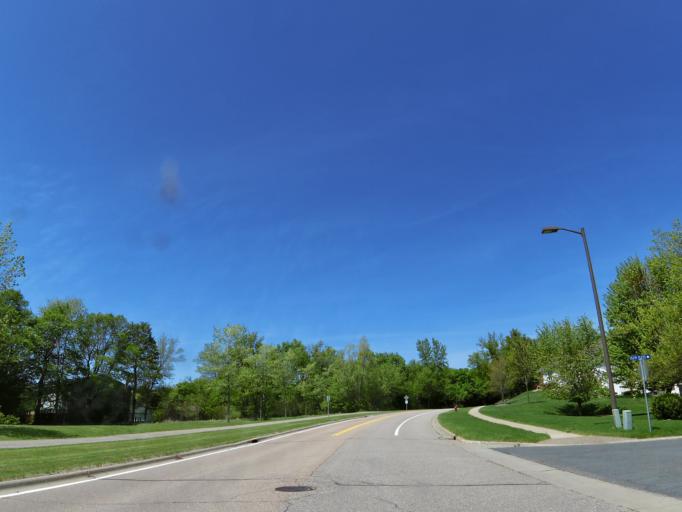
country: US
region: Minnesota
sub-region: Scott County
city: Prior Lake
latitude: 44.7300
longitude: -93.4587
